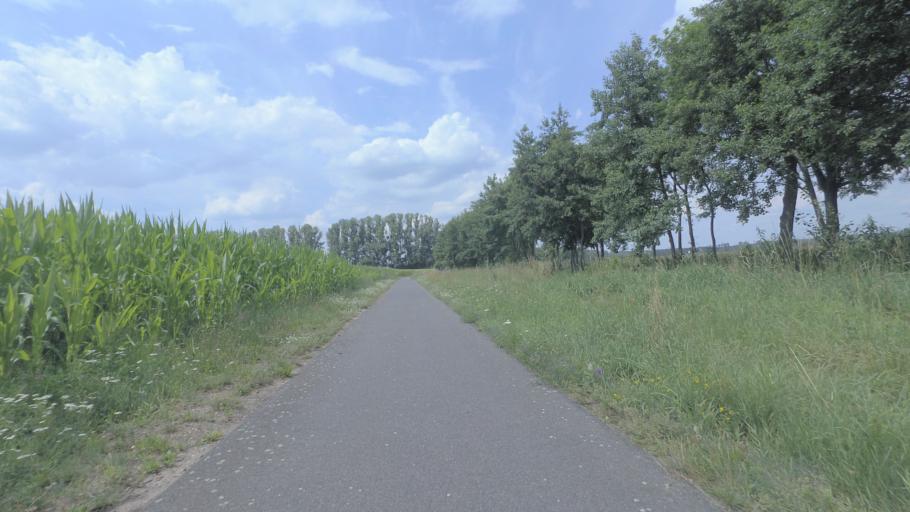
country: DE
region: Brandenburg
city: Luckenwalde
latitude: 52.1089
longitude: 13.2649
